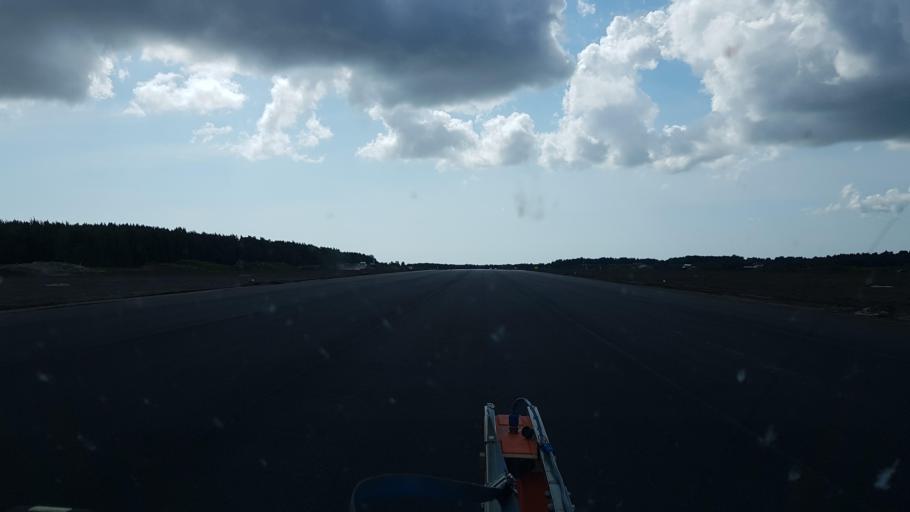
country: EE
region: Paernumaa
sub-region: Sauga vald
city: Sauga
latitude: 58.4215
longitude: 24.4763
